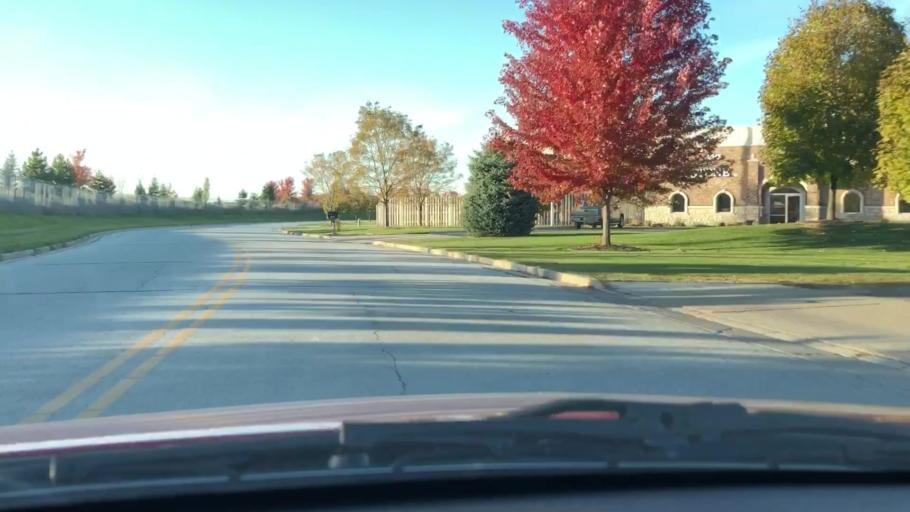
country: US
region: Wisconsin
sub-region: Brown County
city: De Pere
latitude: 44.4317
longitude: -88.1251
